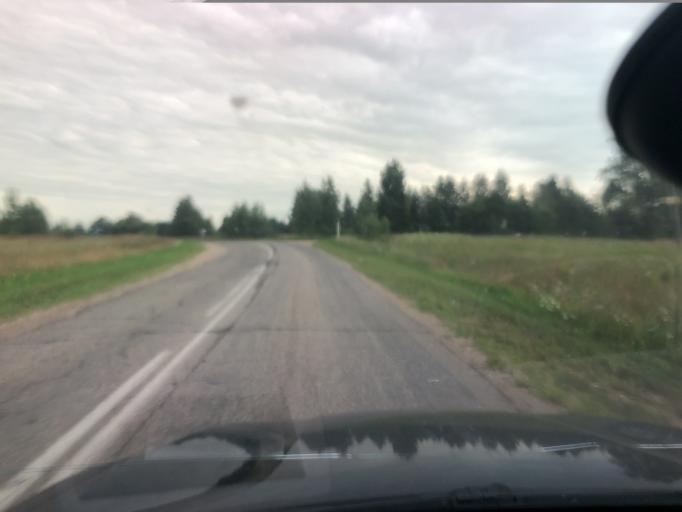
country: RU
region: Jaroslavl
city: Petrovsk
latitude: 57.0008
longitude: 39.0443
